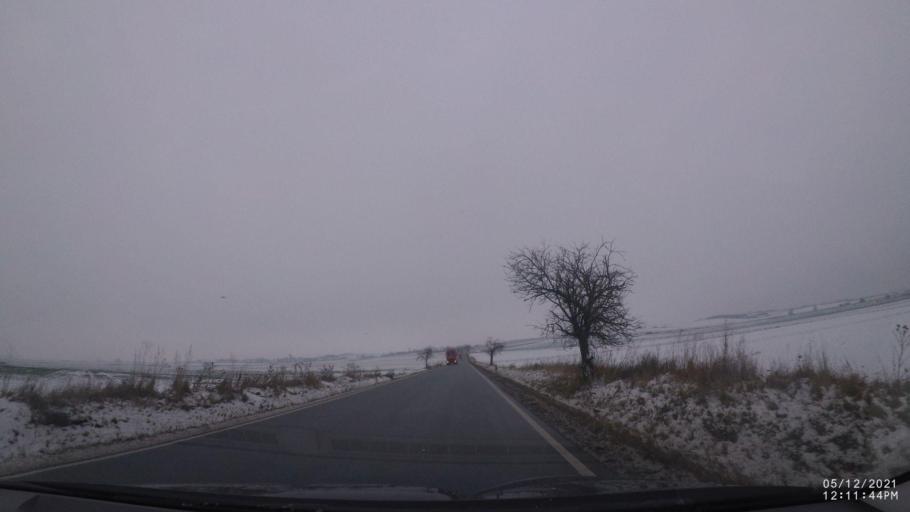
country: CZ
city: Ceske Mezirici
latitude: 50.2887
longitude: 16.0297
